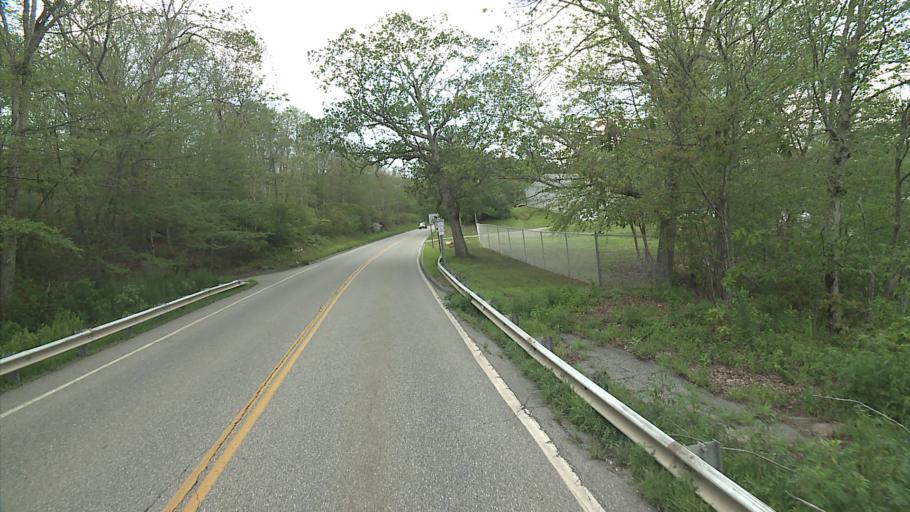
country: US
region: Rhode Island
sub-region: Washington County
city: Hope Valley
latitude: 41.5719
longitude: -71.7922
